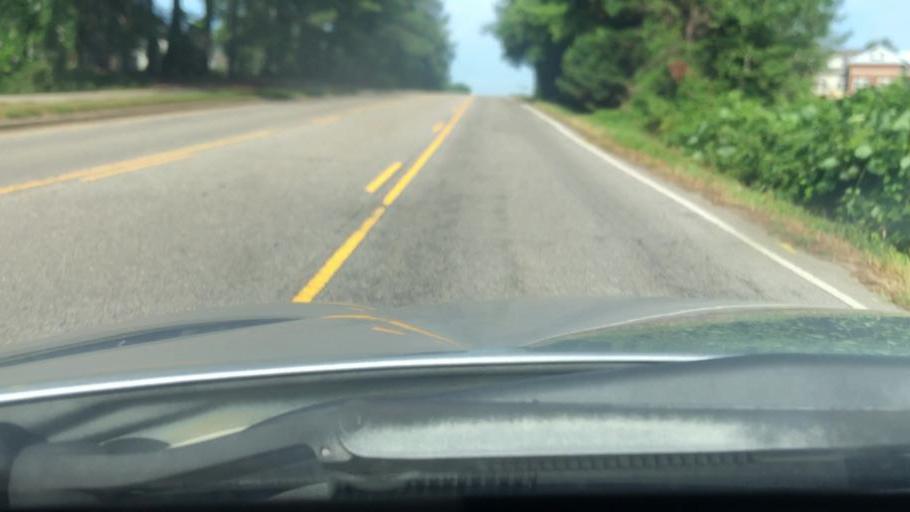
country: US
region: North Carolina
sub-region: Wake County
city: Apex
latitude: 35.7370
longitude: -78.8873
